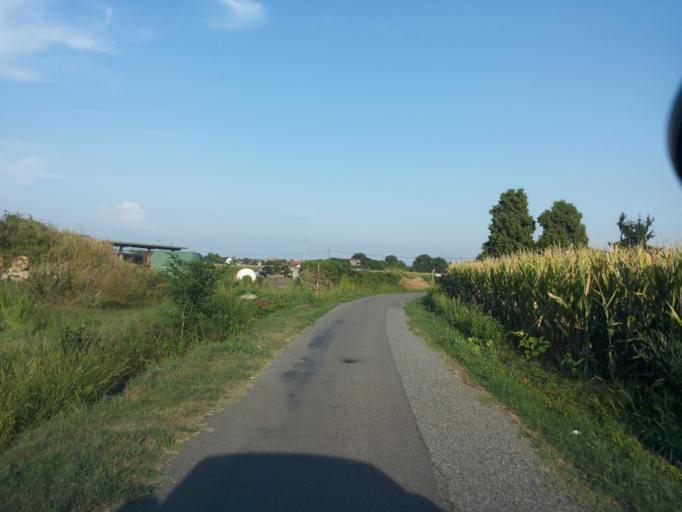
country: IT
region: Piedmont
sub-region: Provincia di Biella
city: Cavaglia
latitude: 45.4015
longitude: 8.0984
